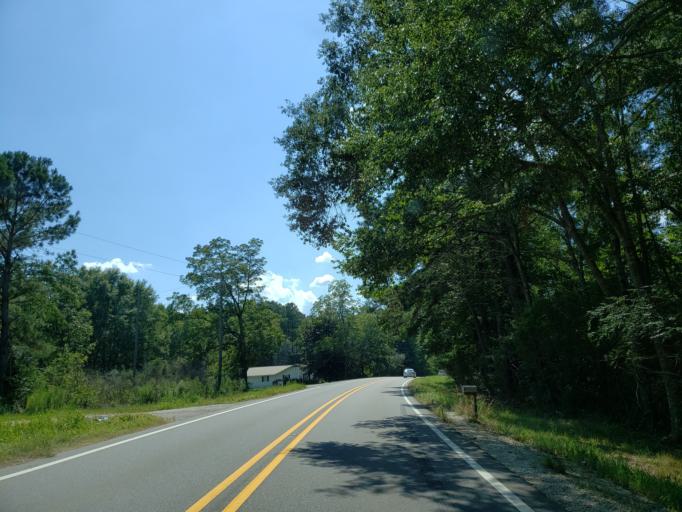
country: US
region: Mississippi
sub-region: Lamar County
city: Sumrall
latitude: 31.3791
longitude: -89.5204
